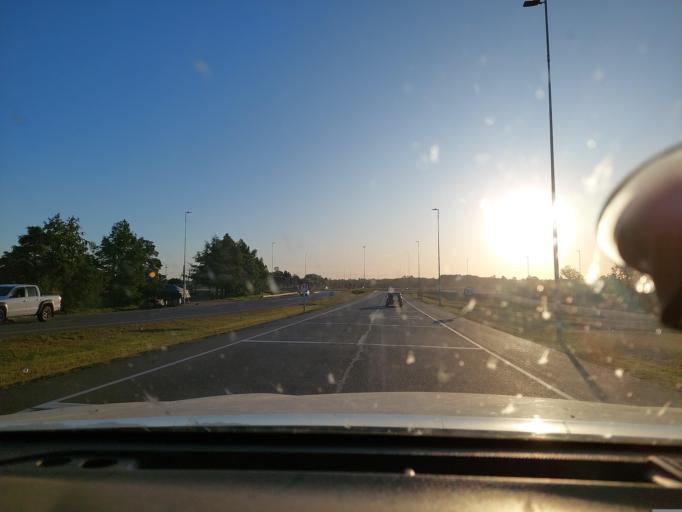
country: UY
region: Canelones
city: Pando
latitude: -34.7099
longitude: -55.9328
